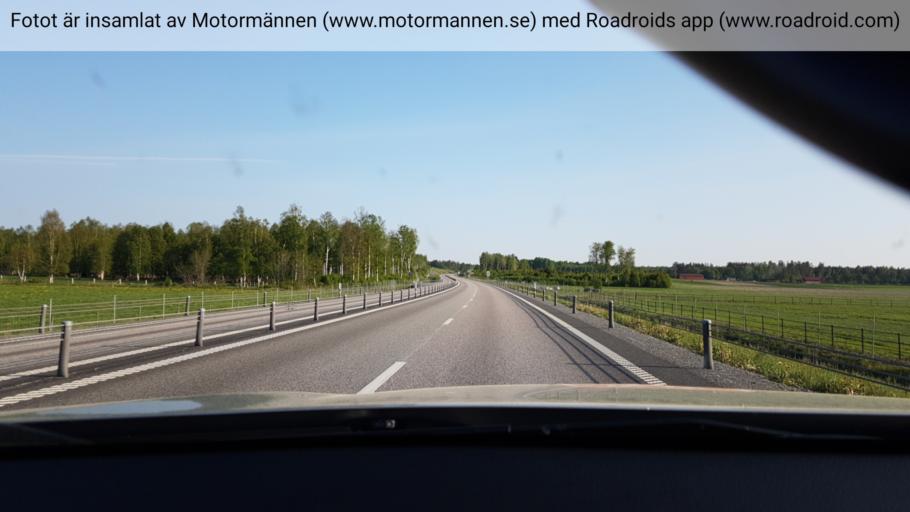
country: SE
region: Uppsala
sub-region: Heby Kommun
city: Heby
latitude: 60.0039
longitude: 16.8512
